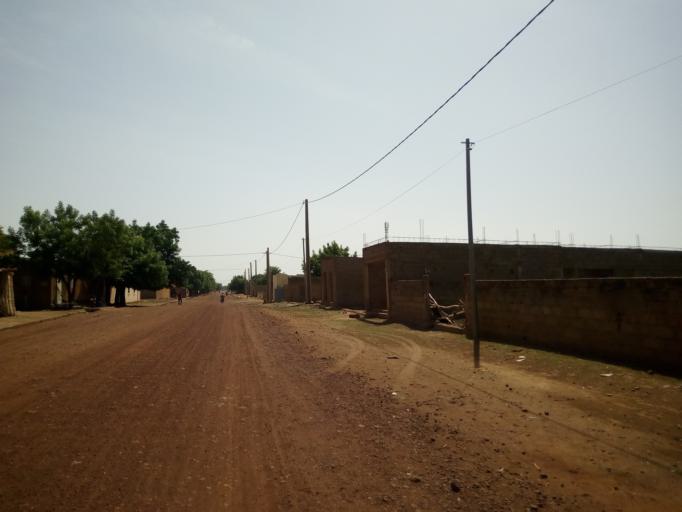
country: ML
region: Segou
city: Segou
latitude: 13.4296
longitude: -6.2107
